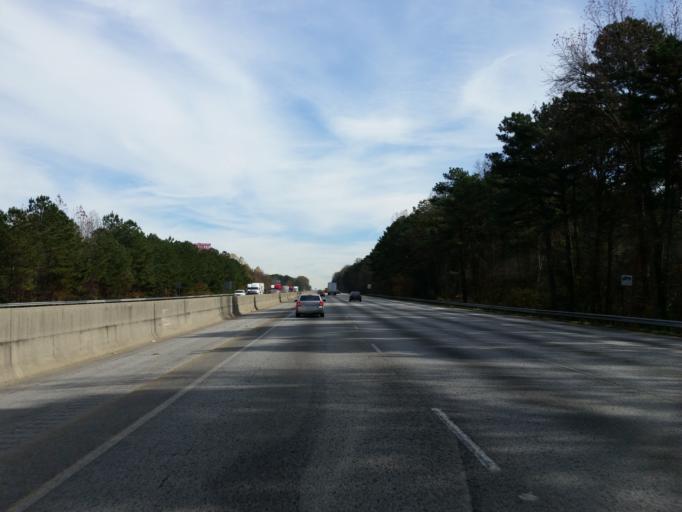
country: US
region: Georgia
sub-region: Cobb County
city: Mableton
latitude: 33.7764
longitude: -84.5983
